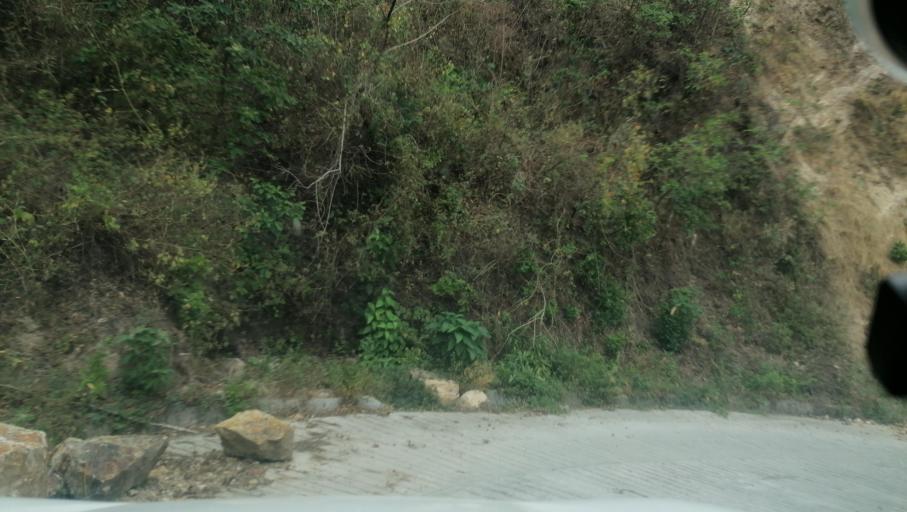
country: MX
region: Chiapas
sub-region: Cacahoatan
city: Benito Juarez
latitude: 15.1623
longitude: -92.1738
